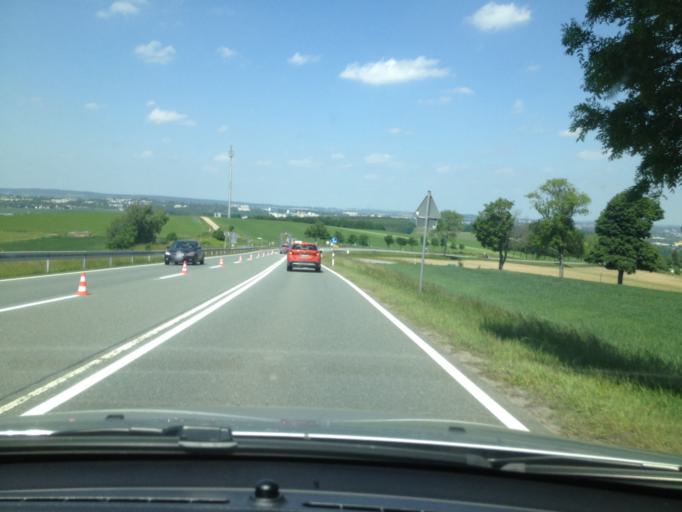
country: DE
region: Saxony
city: Burkhardtsdorf
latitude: 50.7606
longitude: 12.9264
